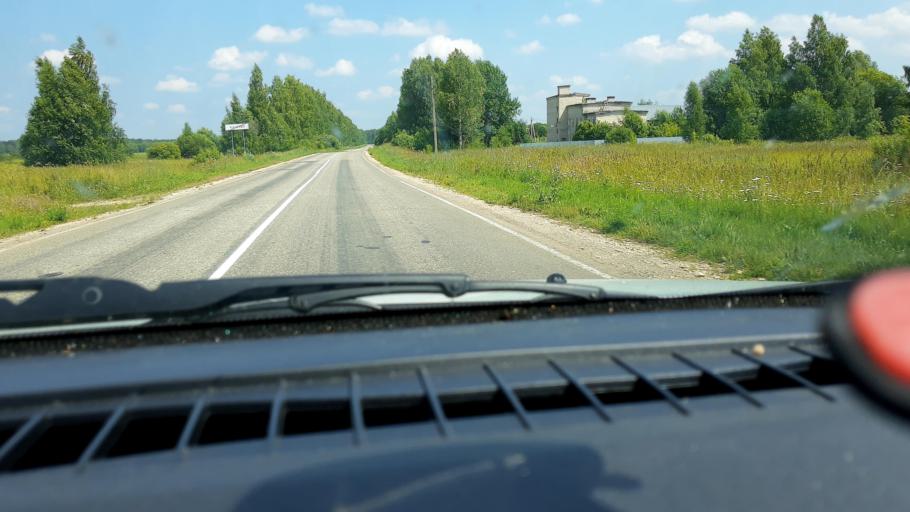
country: RU
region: Nizjnij Novgorod
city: Sharanga
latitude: 57.1298
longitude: 46.5110
